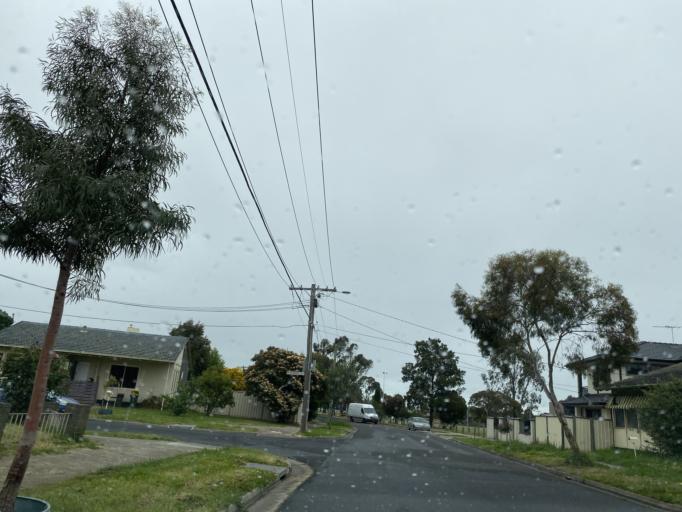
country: AU
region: Victoria
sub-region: Moreland
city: Fawkner
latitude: -37.7127
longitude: 144.9720
